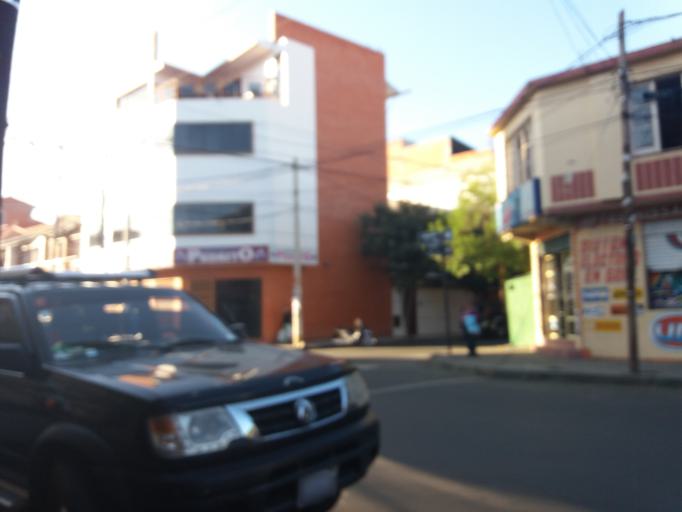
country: BO
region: Tarija
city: Tarija
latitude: -21.5370
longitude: -64.7260
